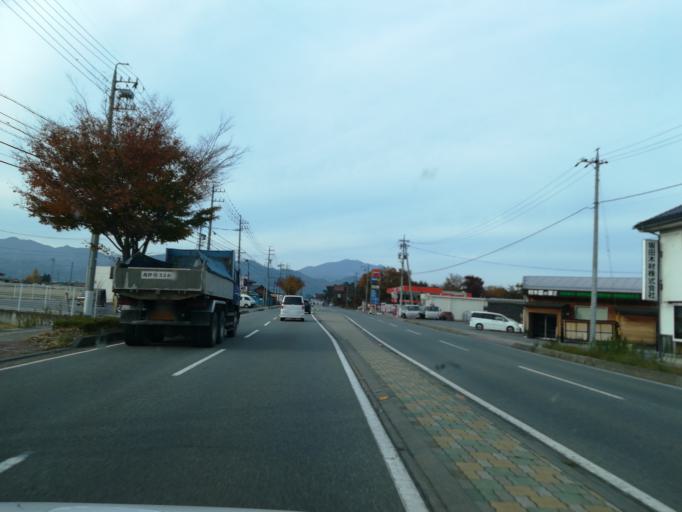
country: JP
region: Nagano
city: Nagano-shi
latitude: 36.5868
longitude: 138.1879
